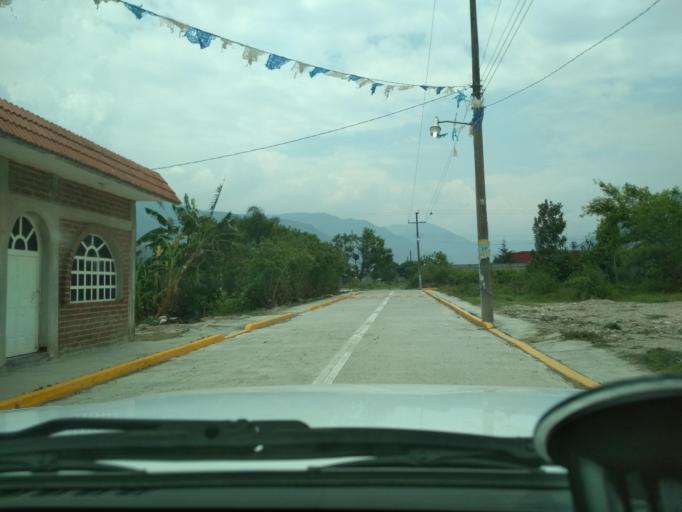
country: MX
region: Veracruz
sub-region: Nogales
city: Taza de Agua Ojo Zarco
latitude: 18.7759
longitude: -97.2098
